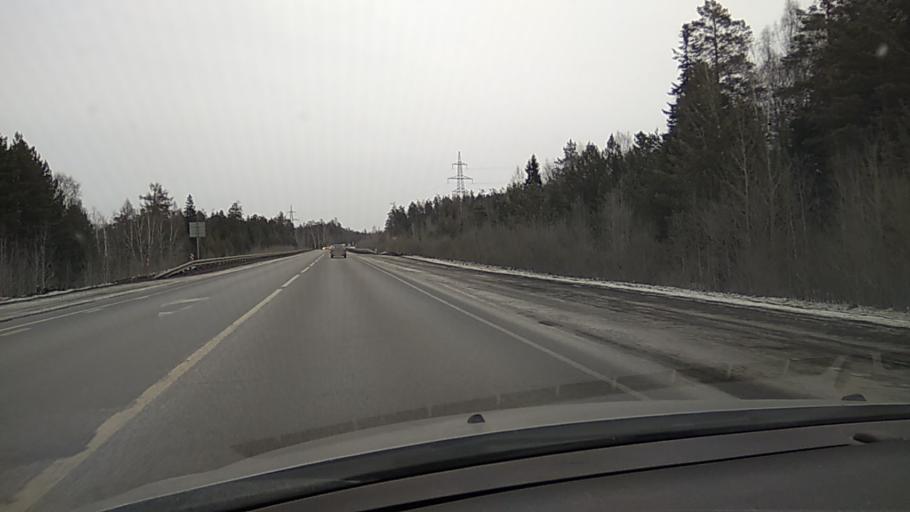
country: RU
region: Sverdlovsk
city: Talitsa
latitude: 56.8471
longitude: 60.0340
